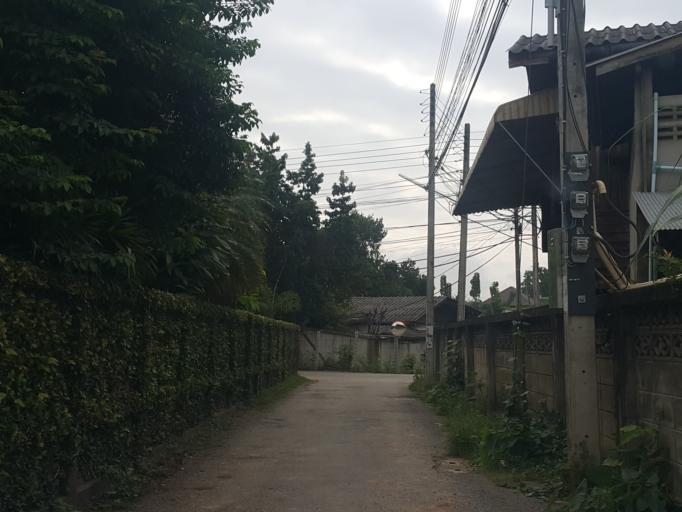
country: TH
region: Lampang
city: Lampang
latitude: 18.2949
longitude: 99.5036
